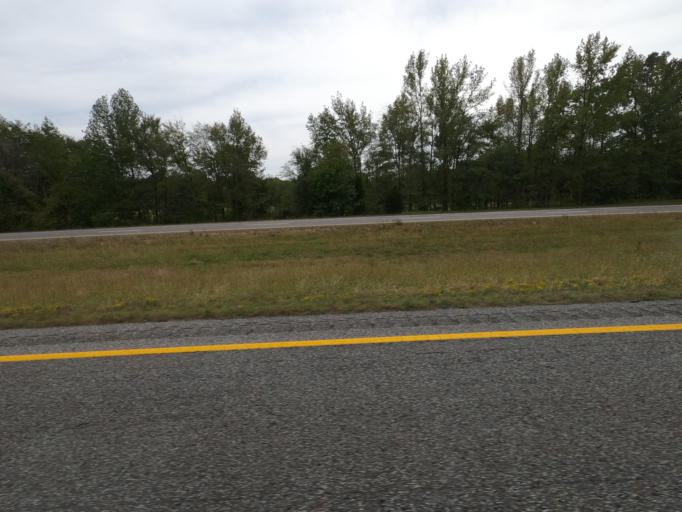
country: US
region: Tennessee
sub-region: Haywood County
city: Brownsville
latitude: 35.5656
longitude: -89.1606
